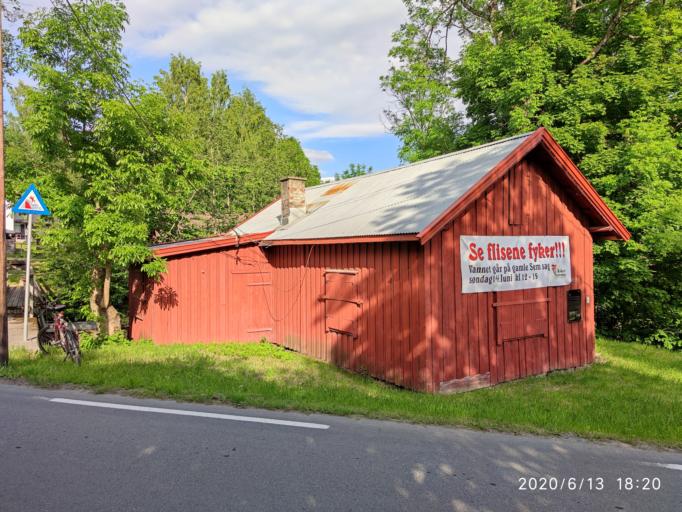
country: NO
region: Akershus
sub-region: Asker
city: Asker
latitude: 59.8515
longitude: 10.4215
